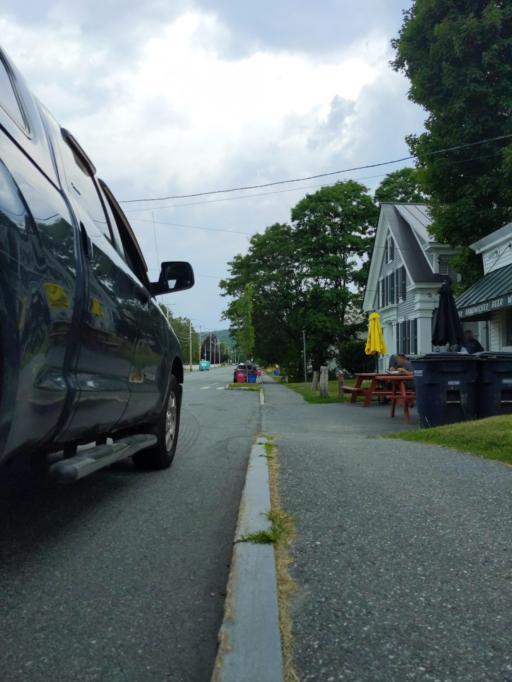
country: US
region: New Hampshire
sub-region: Grafton County
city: Lebanon
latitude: 43.6385
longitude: -72.2479
